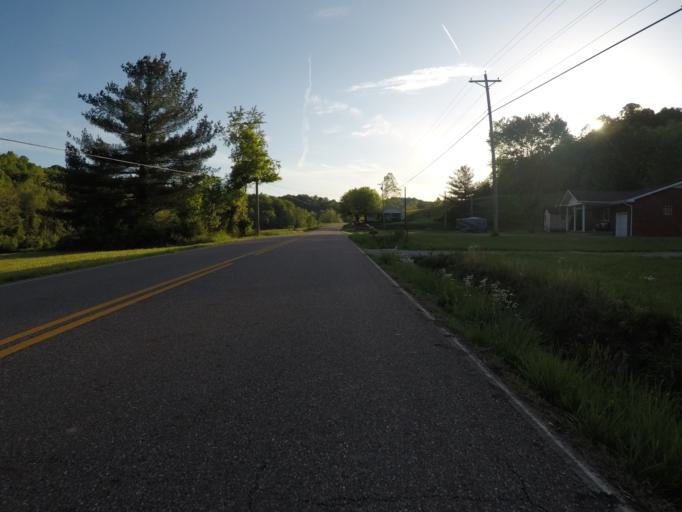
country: US
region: West Virginia
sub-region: Cabell County
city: Huntington
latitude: 38.5550
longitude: -82.4569
